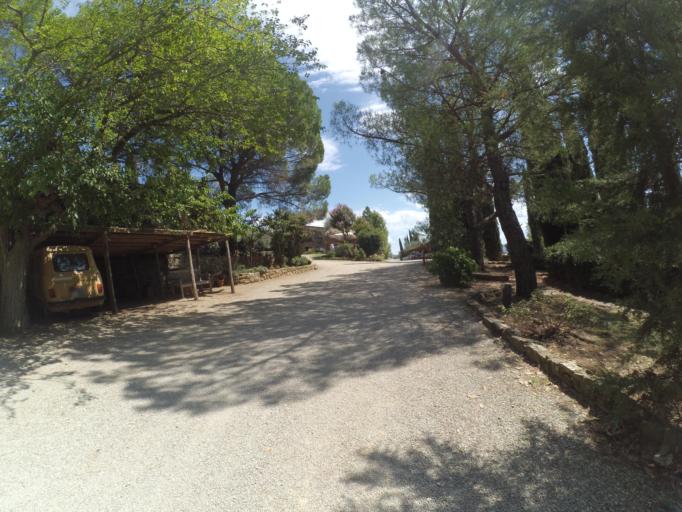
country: IT
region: Tuscany
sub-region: Province of Arezzo
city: Castiglion Fibocchi
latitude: 43.5287
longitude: 11.7797
